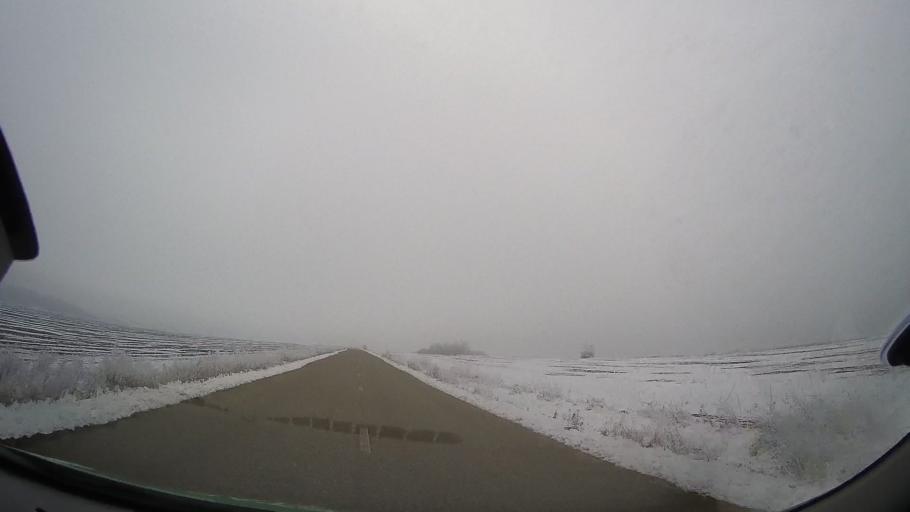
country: RO
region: Vaslui
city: Coroiesti
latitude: 46.2337
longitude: 27.4776
